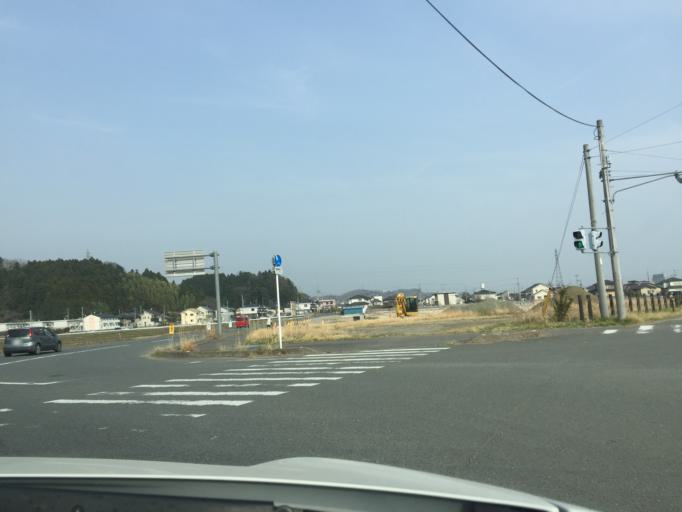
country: JP
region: Fukushima
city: Iwaki
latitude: 36.9594
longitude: 140.8406
